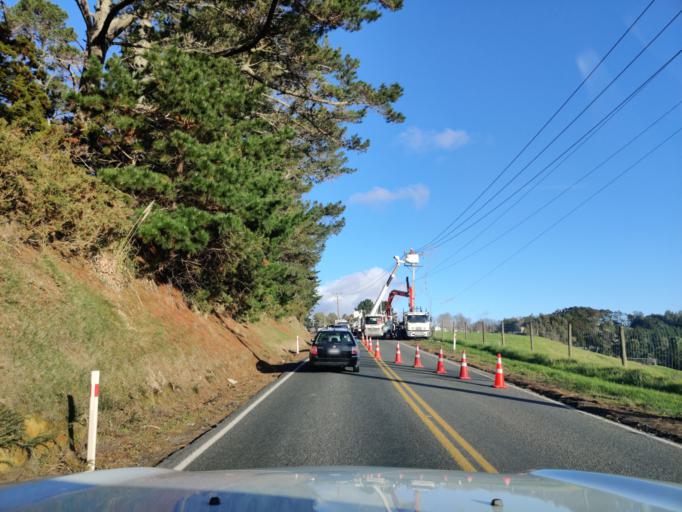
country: NZ
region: Auckland
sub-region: Auckland
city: Red Hill
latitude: -36.9692
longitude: 174.9852
